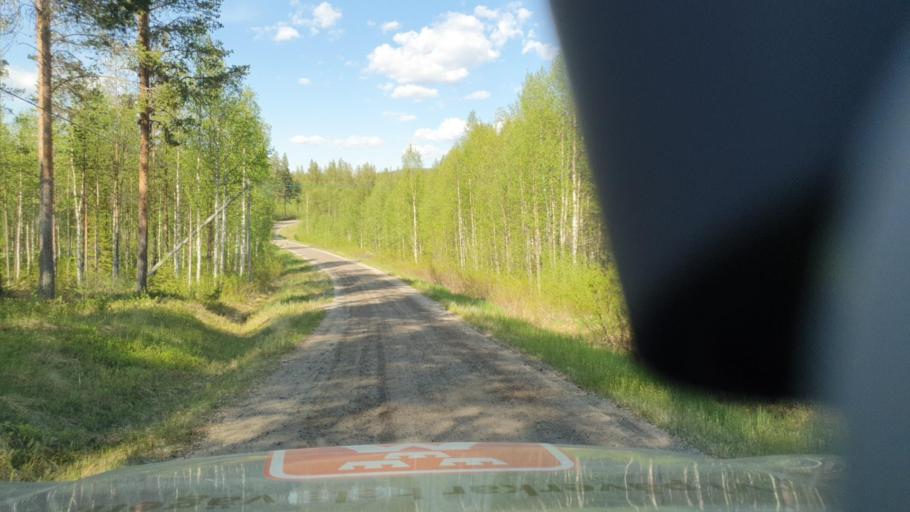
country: SE
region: Norrbotten
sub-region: Overkalix Kommun
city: OEverkalix
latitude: 66.6219
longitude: 22.2329
